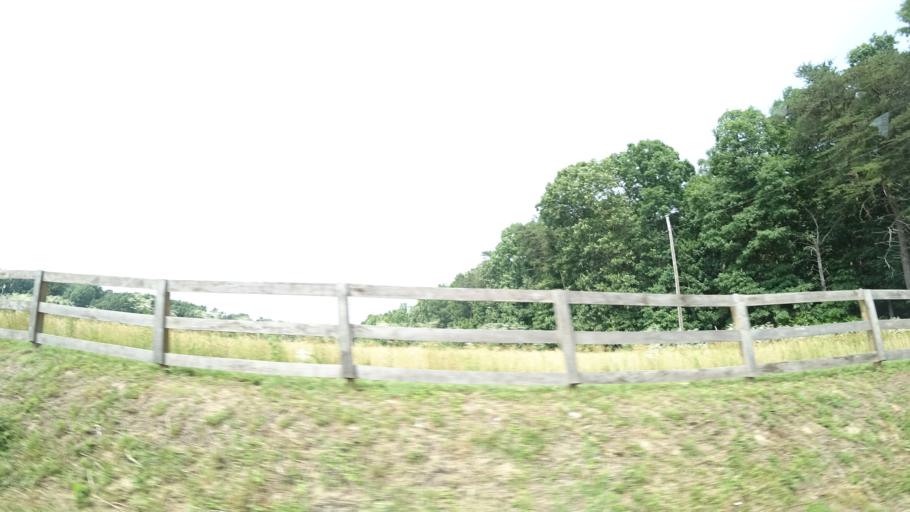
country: US
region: Virginia
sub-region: Spotsylvania County
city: Spotsylvania Courthouse
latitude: 38.1356
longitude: -77.5351
